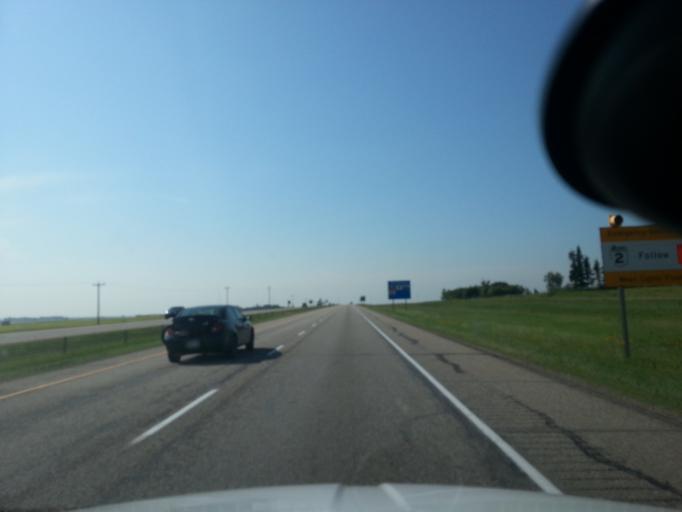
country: CA
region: Alberta
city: Olds
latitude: 51.8087
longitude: -114.0256
